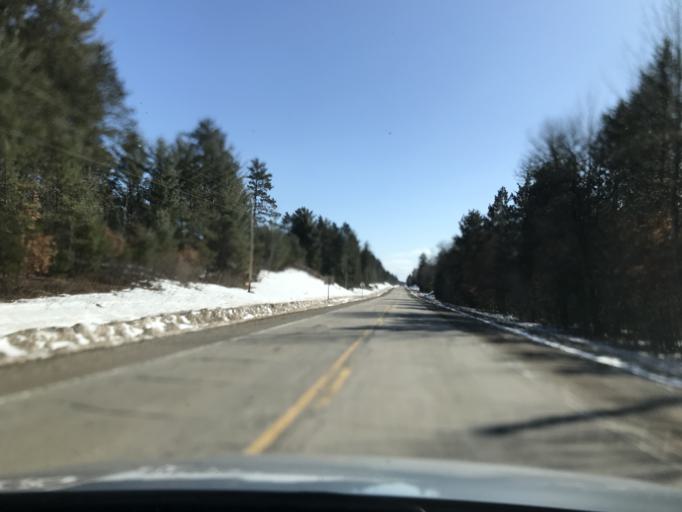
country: US
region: Wisconsin
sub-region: Marinette County
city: Niagara
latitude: 45.3985
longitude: -88.0994
